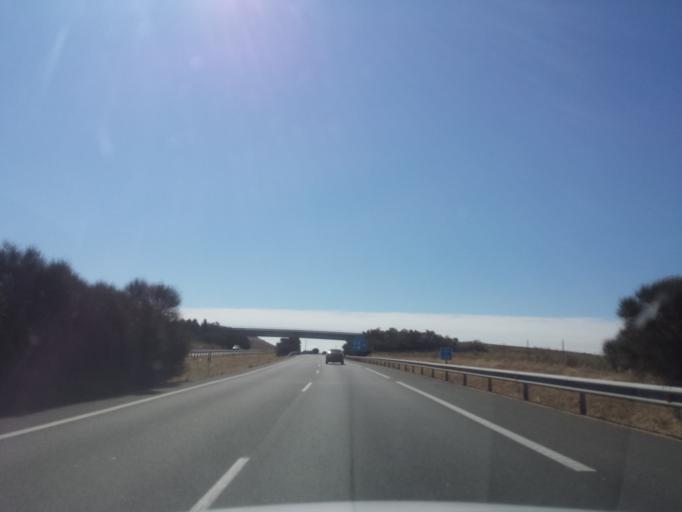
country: ES
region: Castille and Leon
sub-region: Provincia de Valladolid
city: Vega de Valdetronco
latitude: 41.5831
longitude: -5.1084
